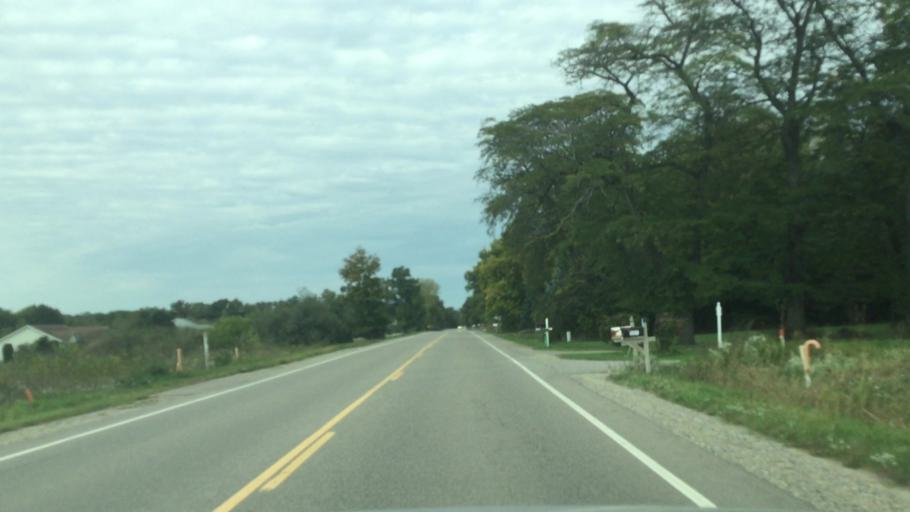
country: US
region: Michigan
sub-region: Livingston County
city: Howell
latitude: 42.6743
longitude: -83.8519
